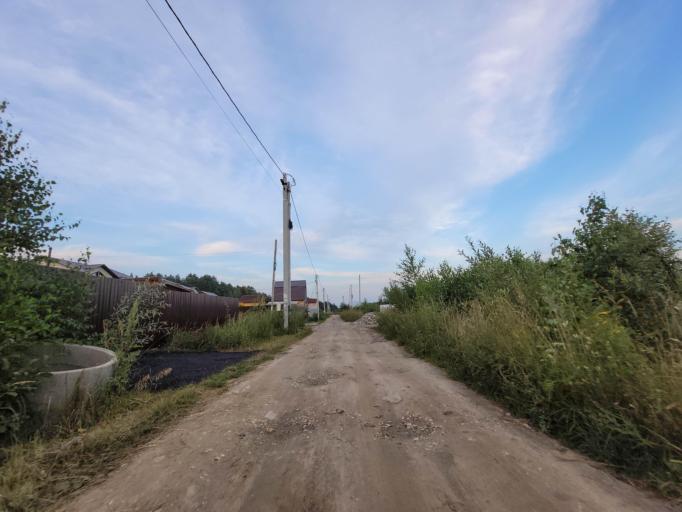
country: RU
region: Moskovskaya
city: Malyshevo
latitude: 55.5354
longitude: 38.3451
